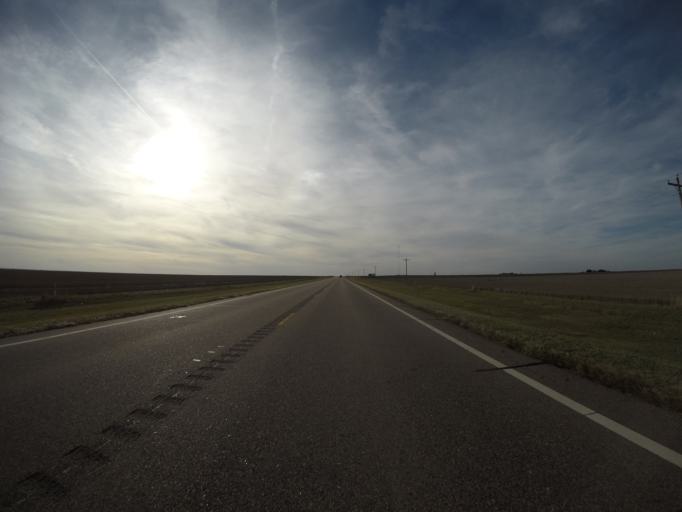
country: US
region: Kansas
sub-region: Cheyenne County
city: Saint Francis
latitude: 39.7566
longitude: -101.6804
